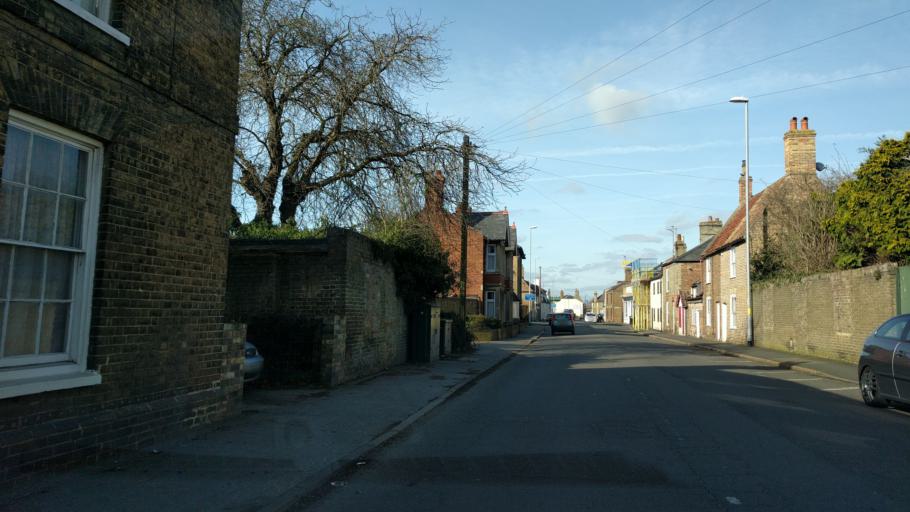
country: GB
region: England
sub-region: Cambridgeshire
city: Chatteris
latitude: 52.4509
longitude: 0.0476
